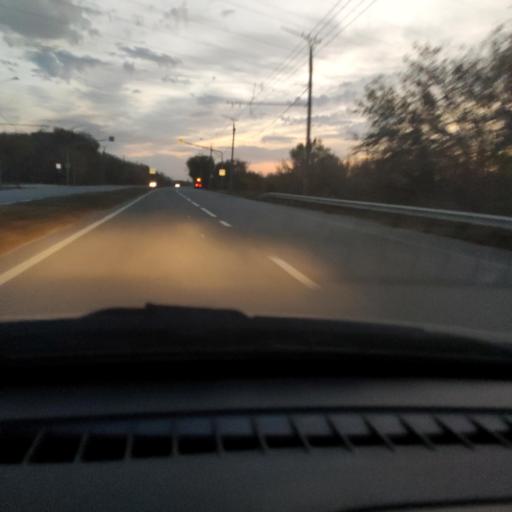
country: RU
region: Samara
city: Zhigulevsk
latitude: 53.5456
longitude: 49.5852
